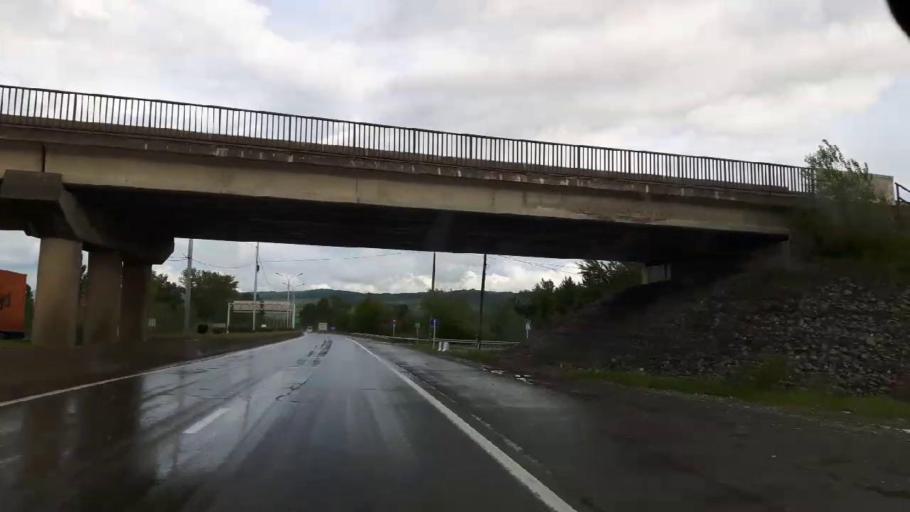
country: GE
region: Shida Kartli
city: Kaspi
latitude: 41.9134
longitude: 44.5603
